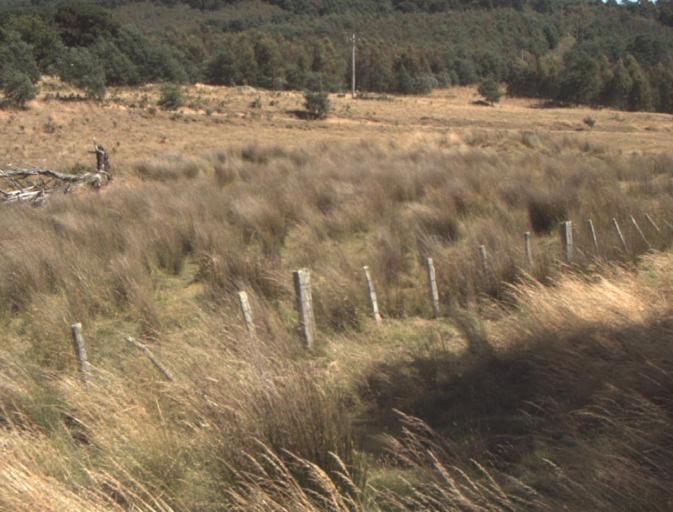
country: AU
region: Tasmania
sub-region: Dorset
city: Scottsdale
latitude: -41.3515
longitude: 147.4406
